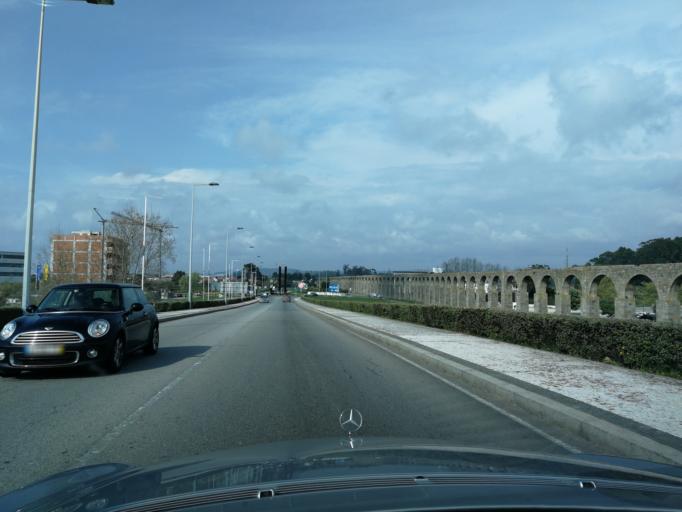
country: PT
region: Porto
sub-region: Vila do Conde
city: Vila do Conde
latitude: 41.3629
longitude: -8.7427
